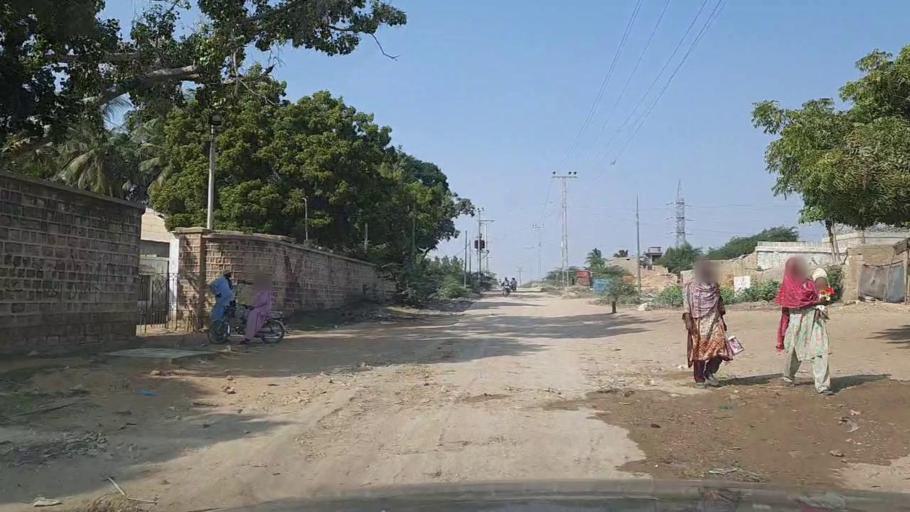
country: PK
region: Sindh
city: Gharo
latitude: 24.7462
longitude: 67.5828
